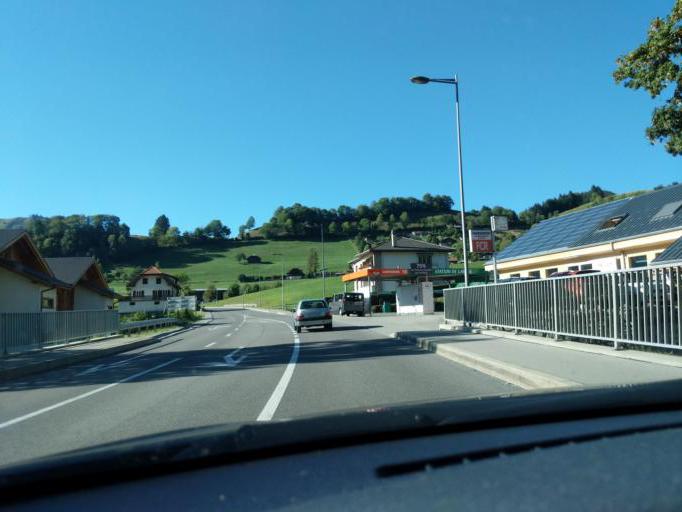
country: CH
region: Fribourg
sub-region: Gruyere District
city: Charmey
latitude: 46.6158
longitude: 7.1700
